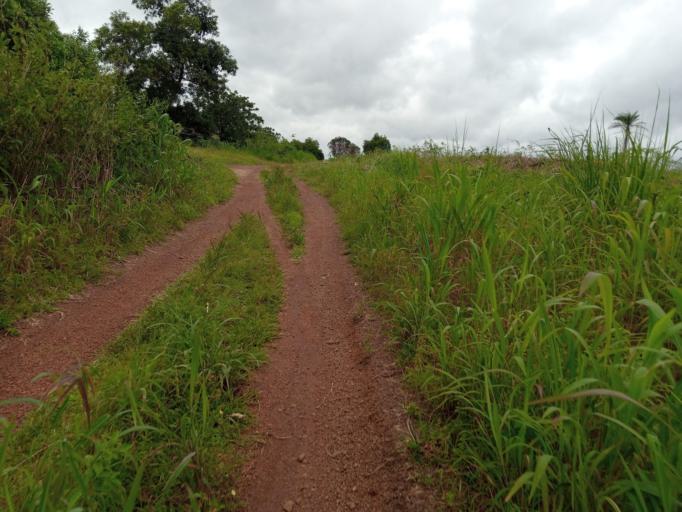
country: SL
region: Southern Province
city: Largo
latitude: 8.1979
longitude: -12.0497
